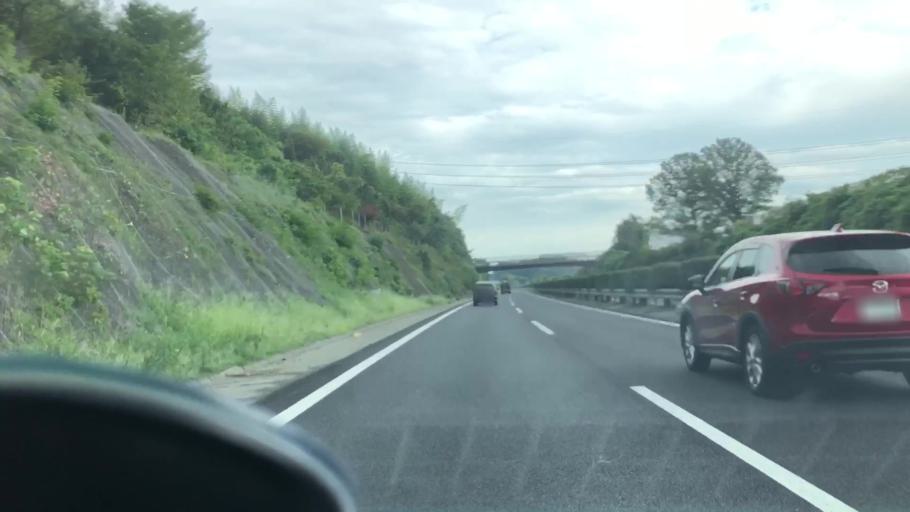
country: JP
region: Hyogo
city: Yashiro
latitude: 34.9380
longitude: 134.8811
